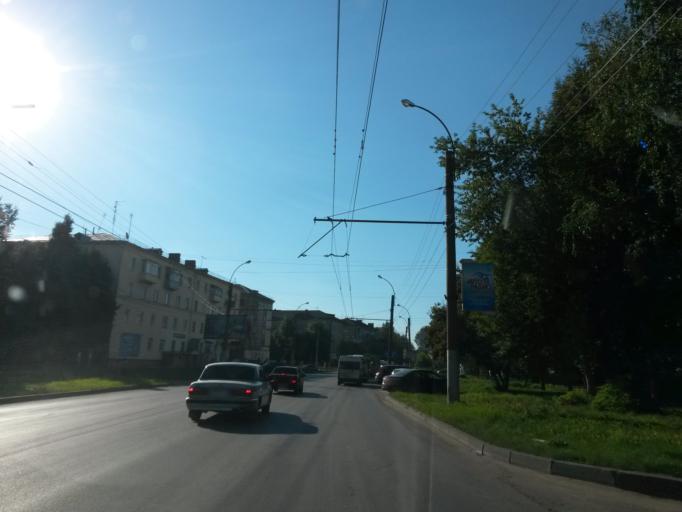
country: RU
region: Ivanovo
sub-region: Gorod Ivanovo
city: Ivanovo
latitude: 56.9837
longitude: 40.9628
